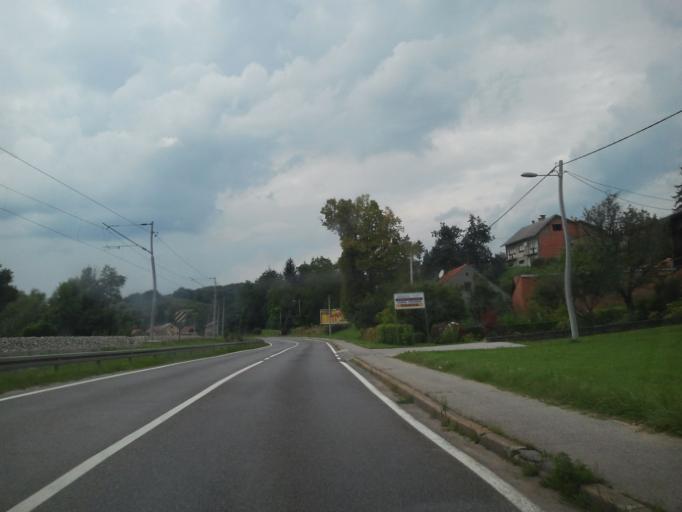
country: HR
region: Karlovacka
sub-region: Grad Karlovac
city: Karlovac
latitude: 45.4647
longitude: 15.5095
